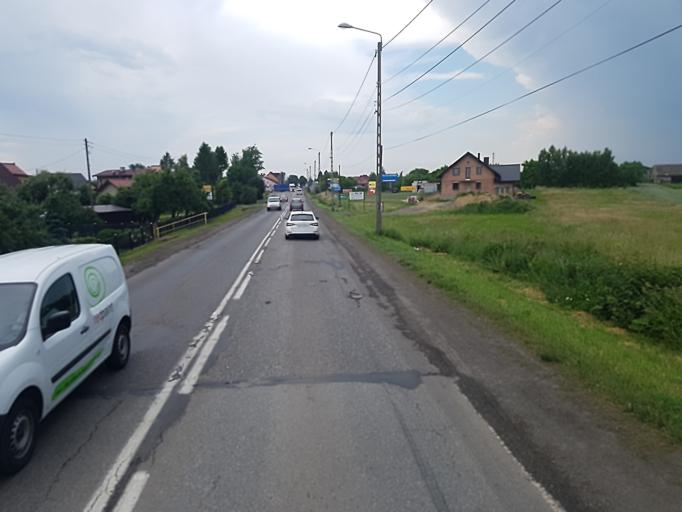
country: PL
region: Silesian Voivodeship
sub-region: Powiat wodzislawski
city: Mszana
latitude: 49.9847
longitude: 18.5085
